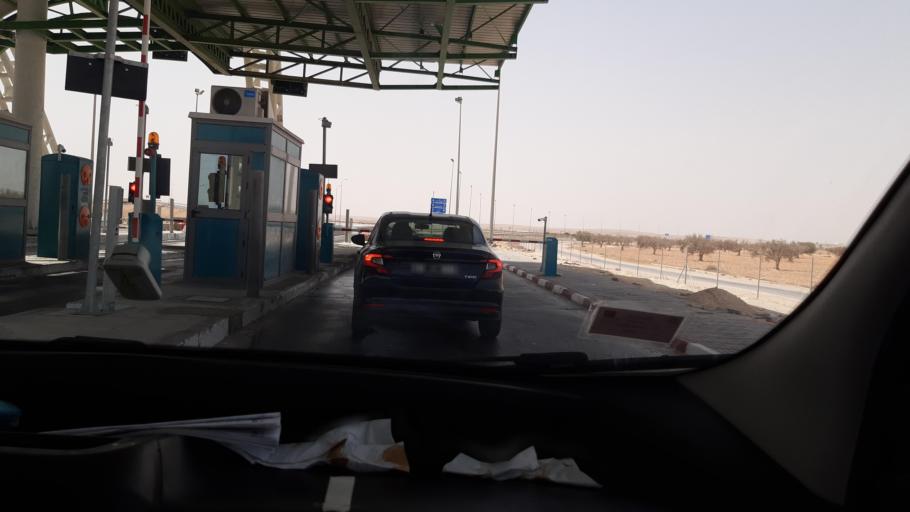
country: TN
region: Qabis
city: Gabes
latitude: 33.8842
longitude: 10.0002
